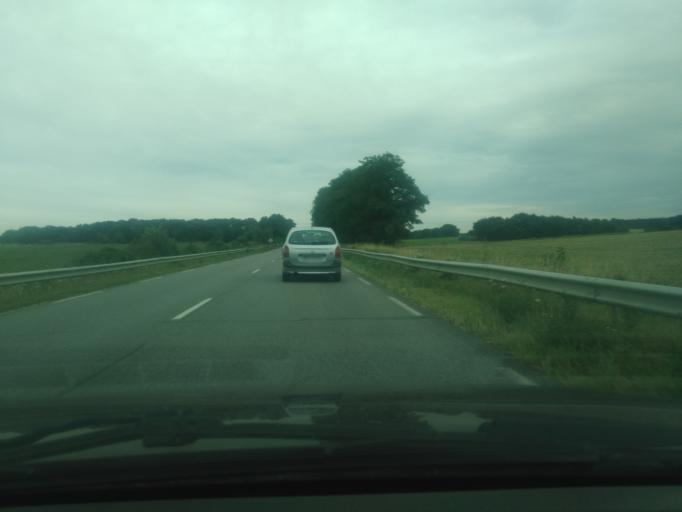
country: FR
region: Centre
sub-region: Departement de l'Indre
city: Le Blanc
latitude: 46.6120
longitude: 1.0062
